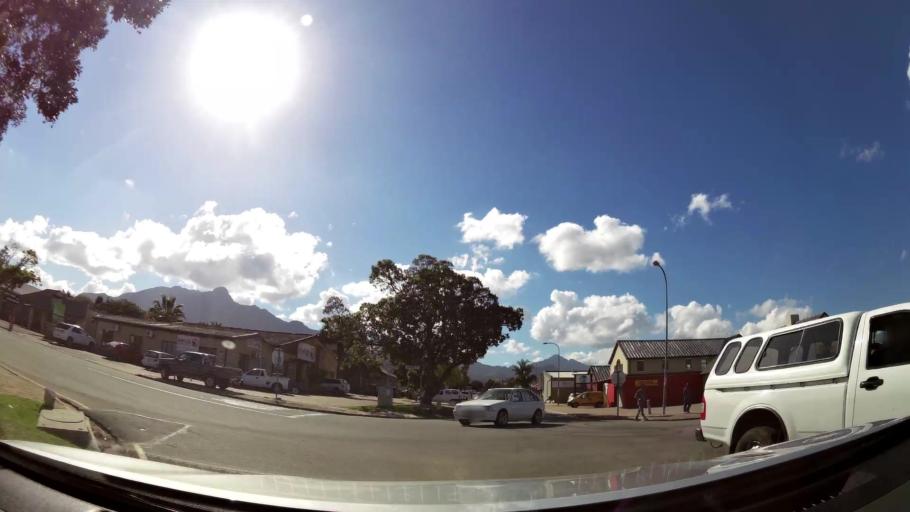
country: ZA
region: Western Cape
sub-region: Eden District Municipality
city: George
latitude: -33.9652
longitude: 22.4642
